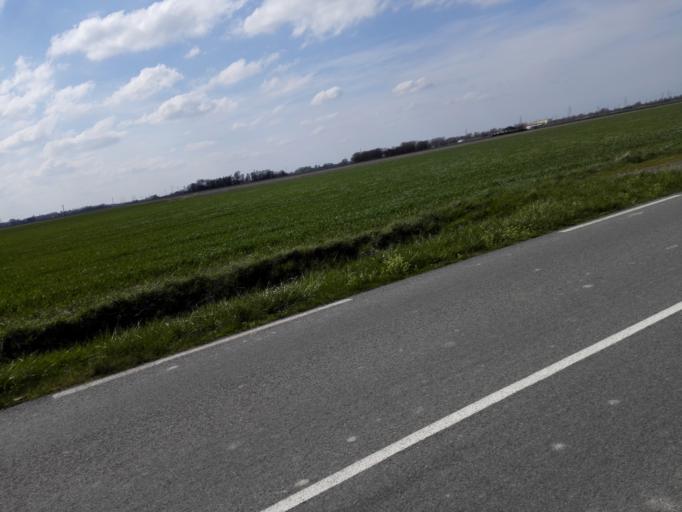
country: FR
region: Nord-Pas-de-Calais
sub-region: Departement du Nord
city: Spycker
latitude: 50.9709
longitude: 2.3156
